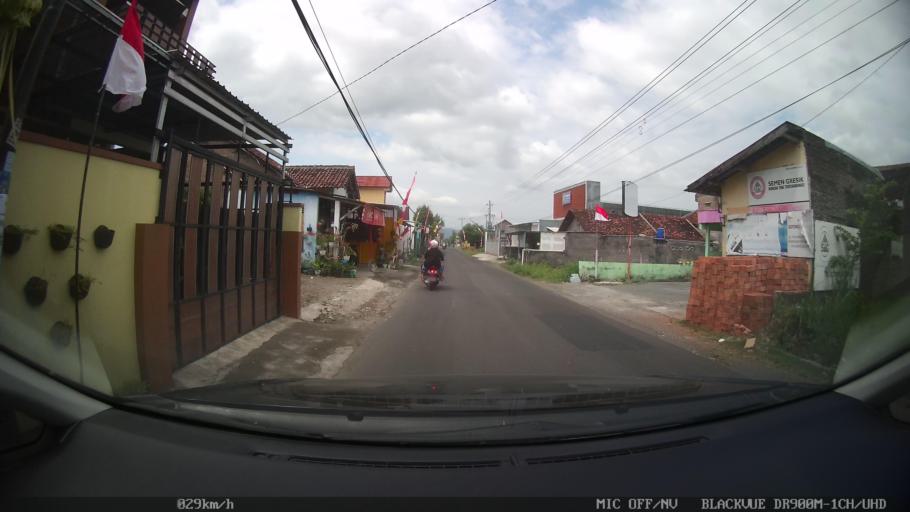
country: ID
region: Daerah Istimewa Yogyakarta
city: Depok
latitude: -7.7790
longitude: 110.4641
